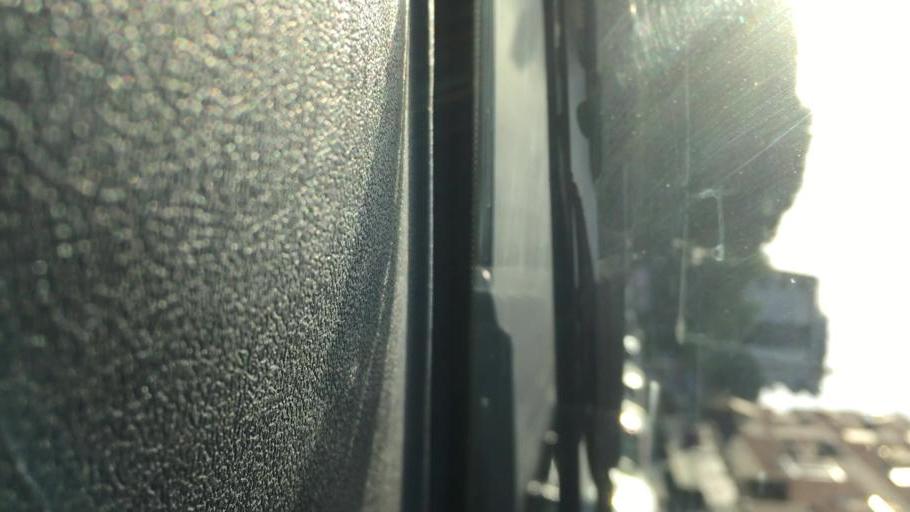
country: IT
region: Latium
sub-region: Citta metropolitana di Roma Capitale
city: Rome
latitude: 41.8380
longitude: 12.4850
